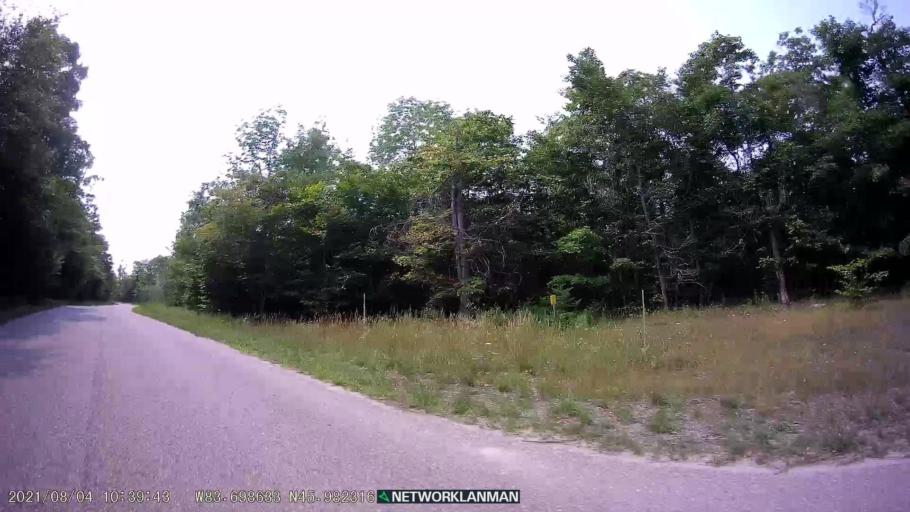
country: CA
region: Ontario
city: Thessalon
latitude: 45.9814
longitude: -83.6993
